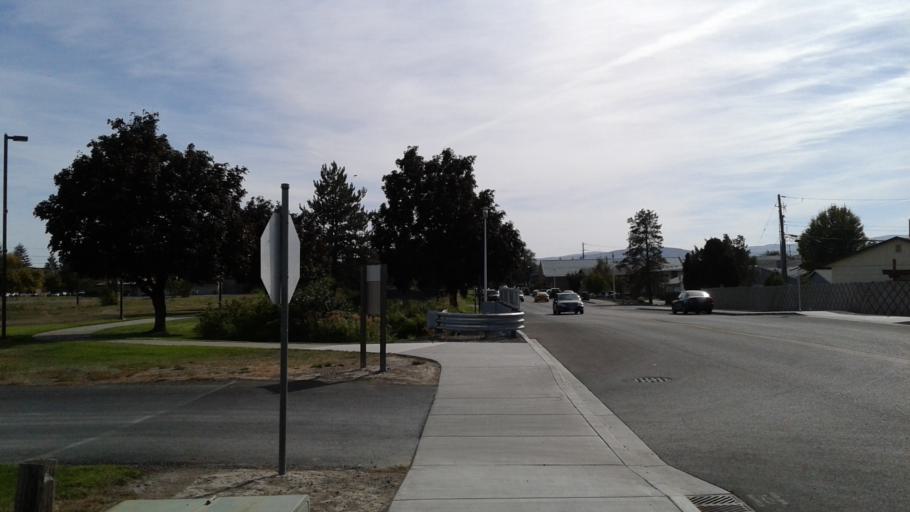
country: US
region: Washington
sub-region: Kittitas County
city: Ellensburg
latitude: 47.0088
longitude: -120.5433
